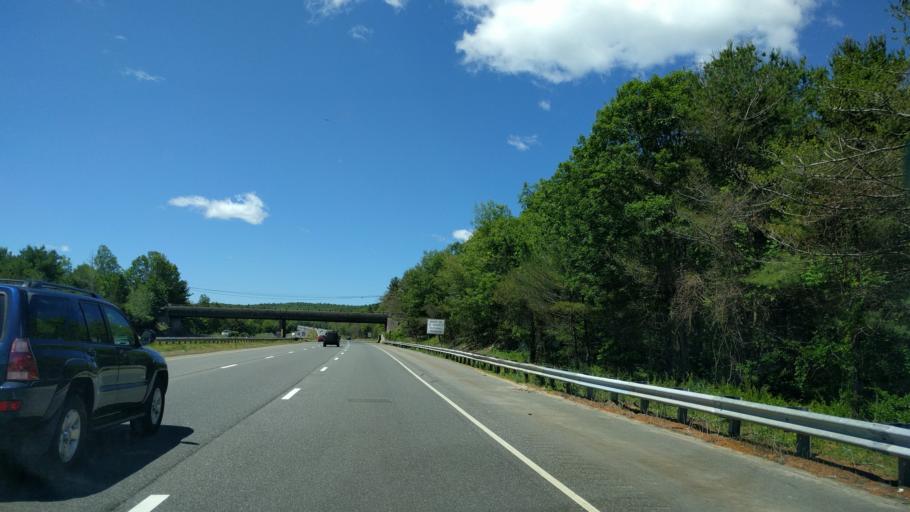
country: US
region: Massachusetts
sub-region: Hampden County
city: Holland
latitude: 42.0262
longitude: -72.1415
